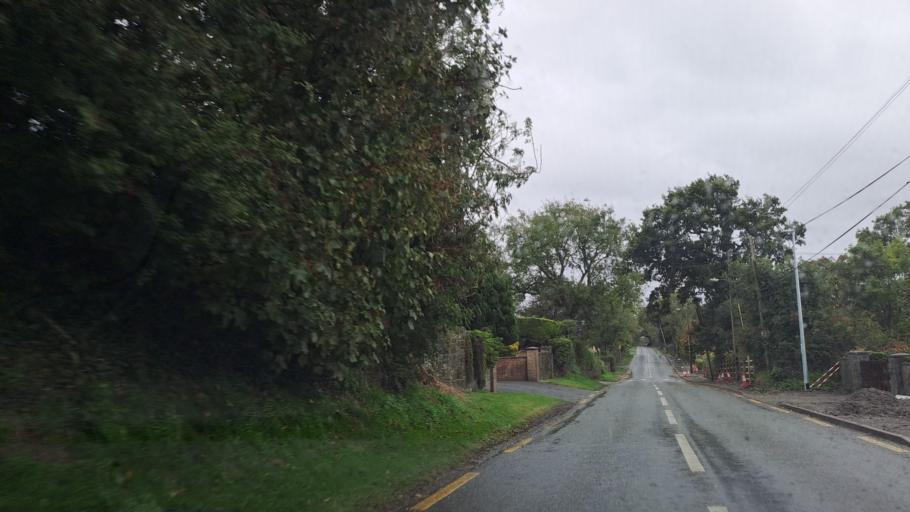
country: IE
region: Leinster
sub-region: Lu
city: Dundalk
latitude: 53.9702
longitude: -6.4836
